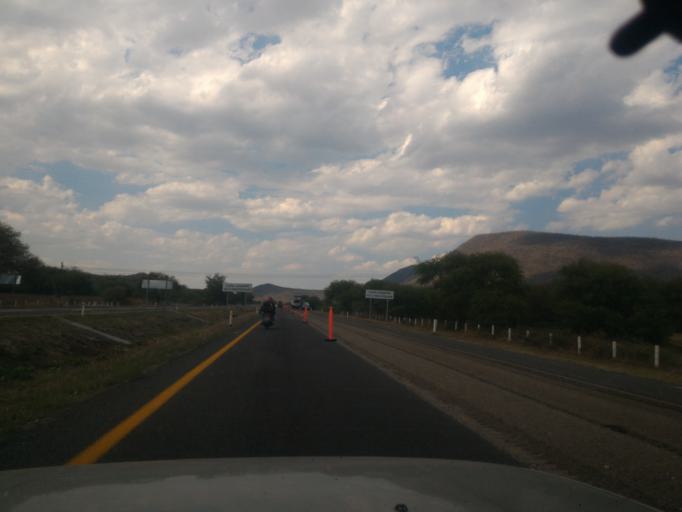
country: MX
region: Jalisco
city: Zacoalco de Torres
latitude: 20.1710
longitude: -103.5063
